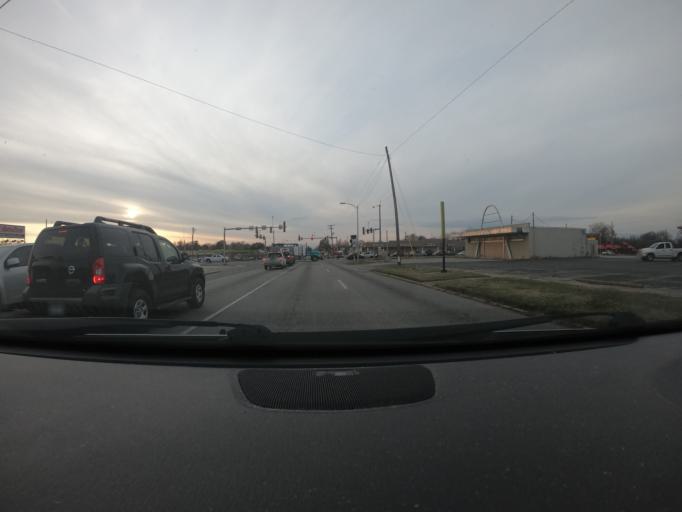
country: US
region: Arkansas
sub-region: Benton County
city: Rogers
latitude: 36.3335
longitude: -94.1248
